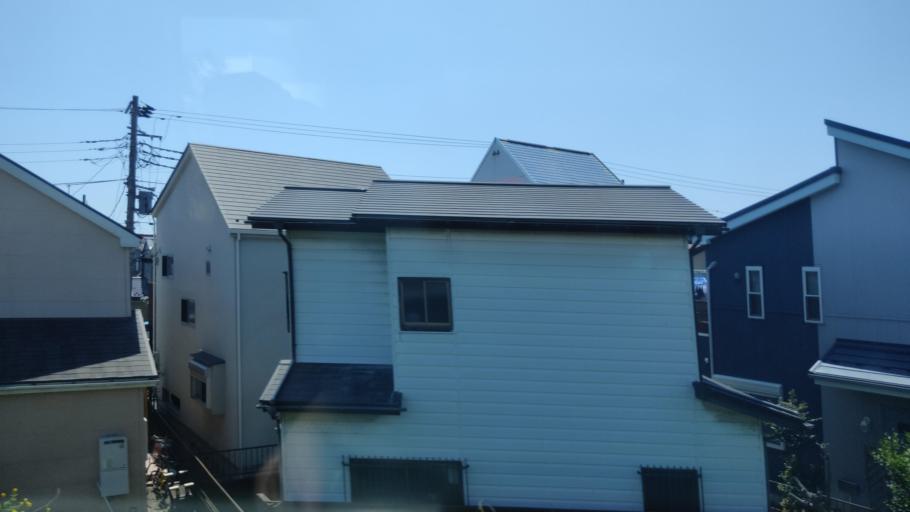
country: JP
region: Kanagawa
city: Chigasaki
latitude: 35.3290
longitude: 139.3836
